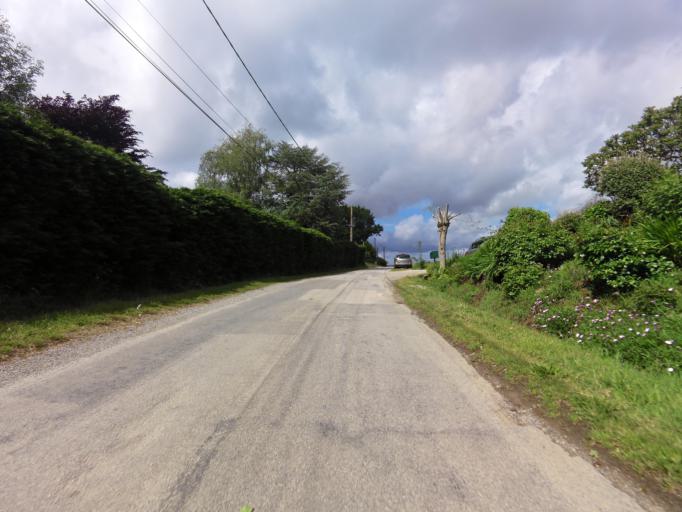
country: FR
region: Brittany
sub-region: Departement du Morbihan
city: Plougoumelen
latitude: 47.6349
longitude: -2.9149
